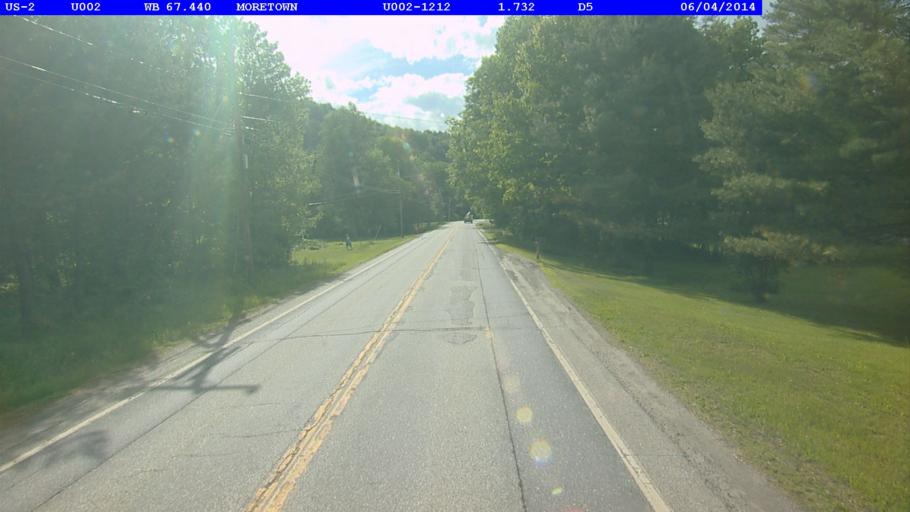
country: US
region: Vermont
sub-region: Washington County
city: Waterbury
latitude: 44.3121
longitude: -72.7199
